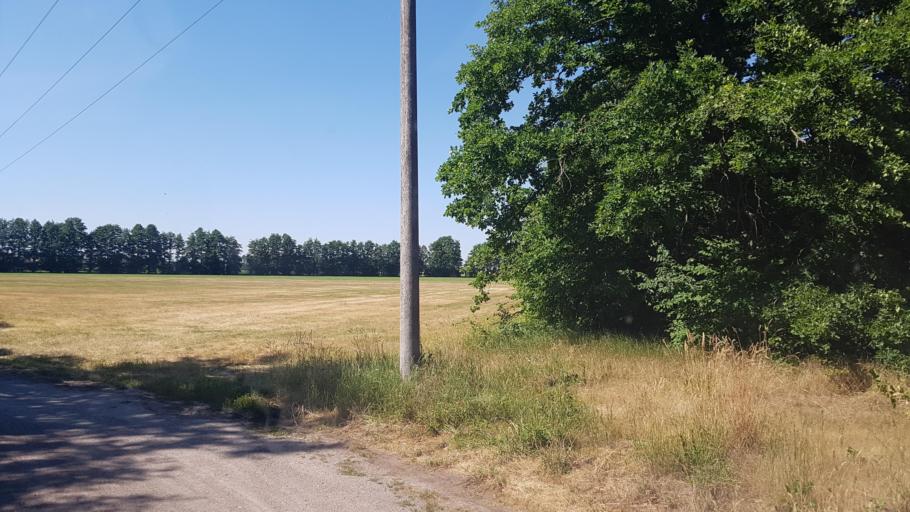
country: DE
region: Saxony-Anhalt
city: Seyda
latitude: 51.8521
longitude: 12.8989
